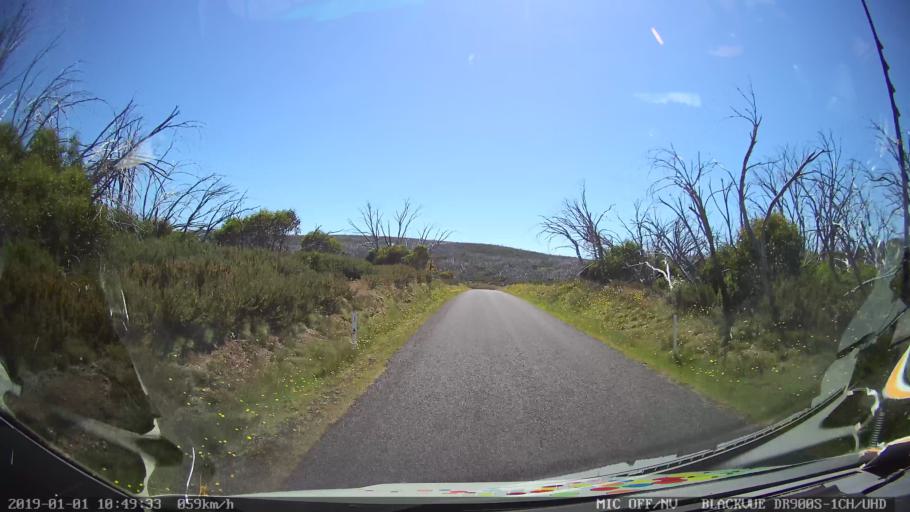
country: AU
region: New South Wales
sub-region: Snowy River
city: Jindabyne
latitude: -36.0344
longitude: 148.3715
